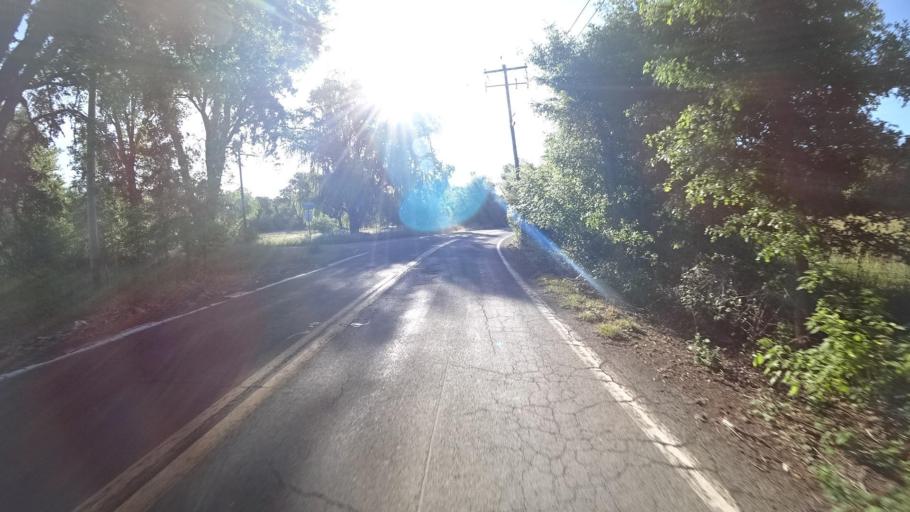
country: US
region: California
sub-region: Lake County
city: North Lakeport
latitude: 39.0945
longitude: -122.9626
